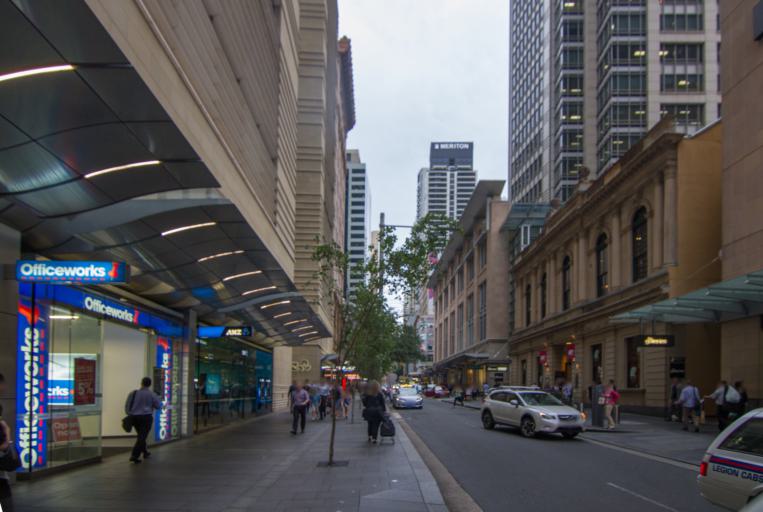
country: AU
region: New South Wales
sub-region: City of Sydney
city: Sydney
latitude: -33.8720
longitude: 151.2083
